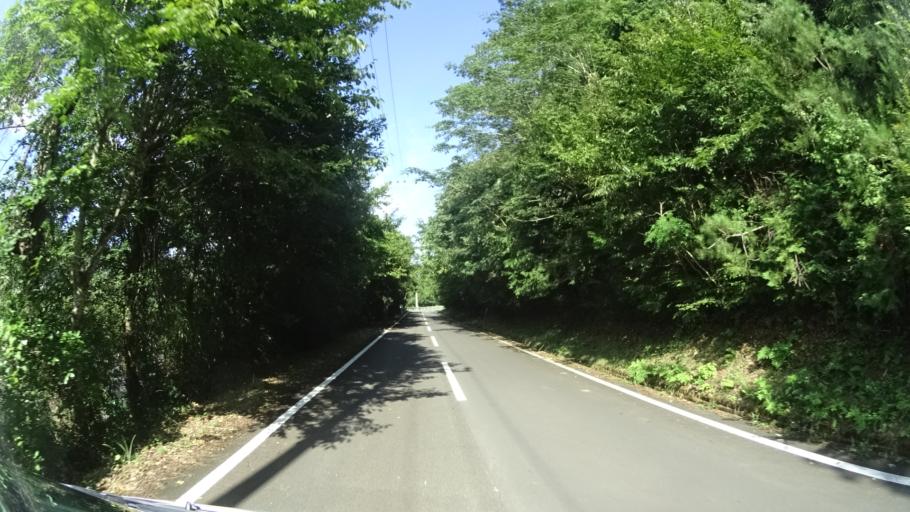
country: JP
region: Kyoto
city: Ayabe
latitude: 35.2949
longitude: 135.3240
